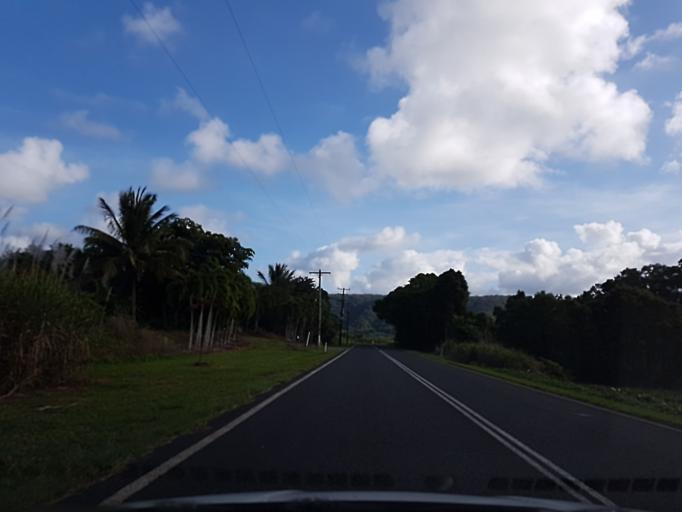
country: AU
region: Queensland
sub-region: Cairns
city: Port Douglas
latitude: -16.2759
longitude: 145.3890
